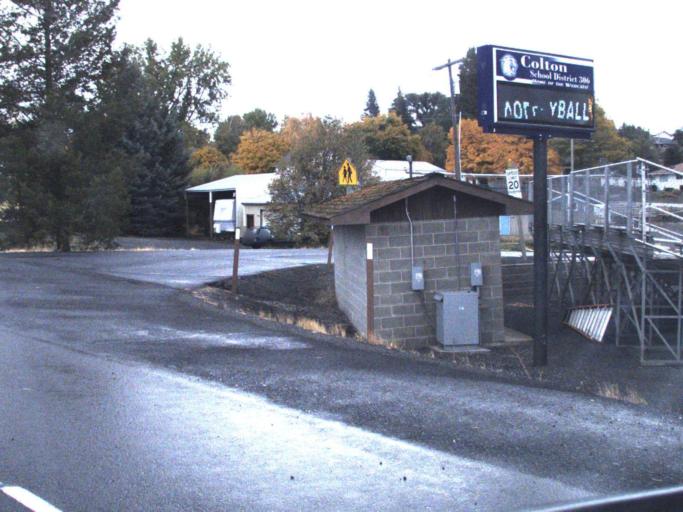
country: US
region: Washington
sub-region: Whitman County
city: Pullman
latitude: 46.5680
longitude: -117.1302
